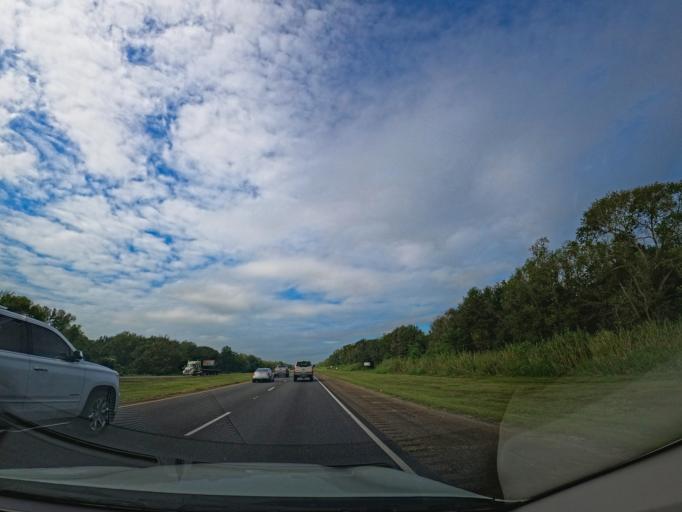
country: US
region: Louisiana
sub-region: Saint Mary Parish
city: Berwick
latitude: 29.6893
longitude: -91.2367
